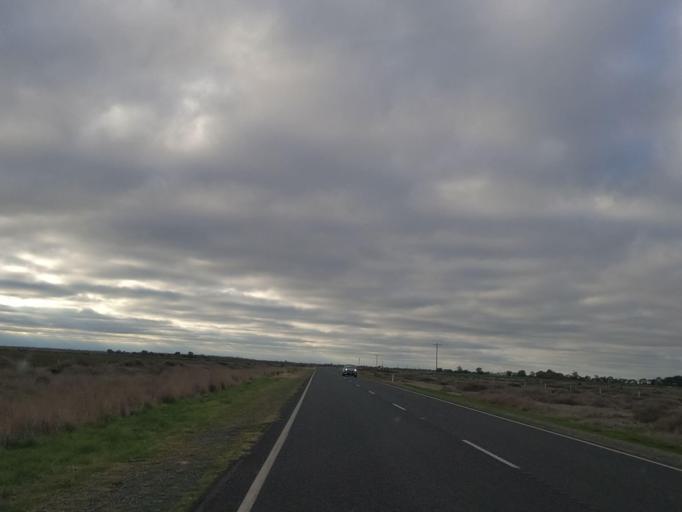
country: AU
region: Victoria
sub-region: Swan Hill
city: Swan Hill
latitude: -35.8456
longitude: 143.9381
